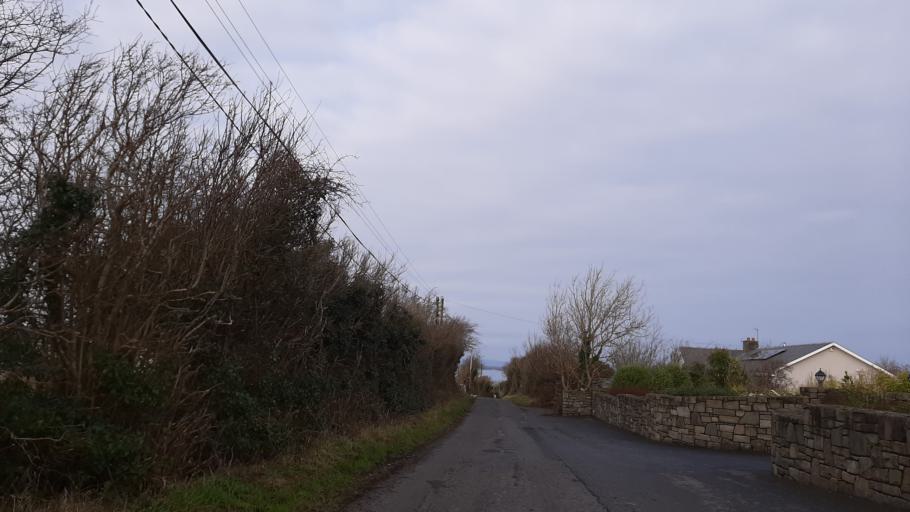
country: IE
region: Connaught
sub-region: County Galway
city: Gaillimh
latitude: 53.3149
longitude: -9.0529
